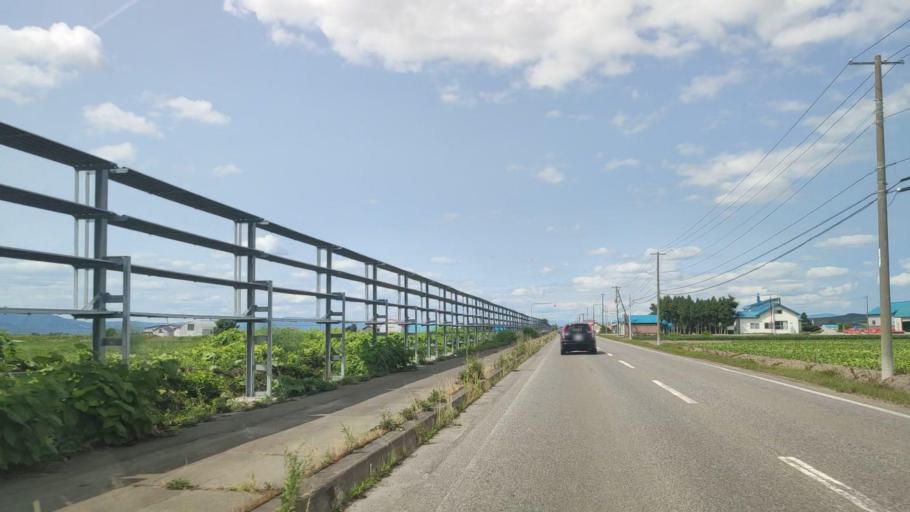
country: JP
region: Hokkaido
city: Nayoro
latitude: 44.1924
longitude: 142.4159
